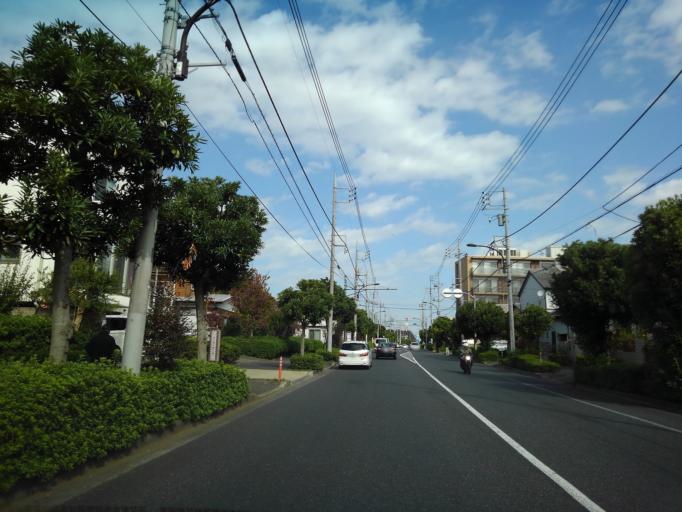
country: JP
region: Tokyo
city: Kokubunji
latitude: 35.7255
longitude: 139.4977
